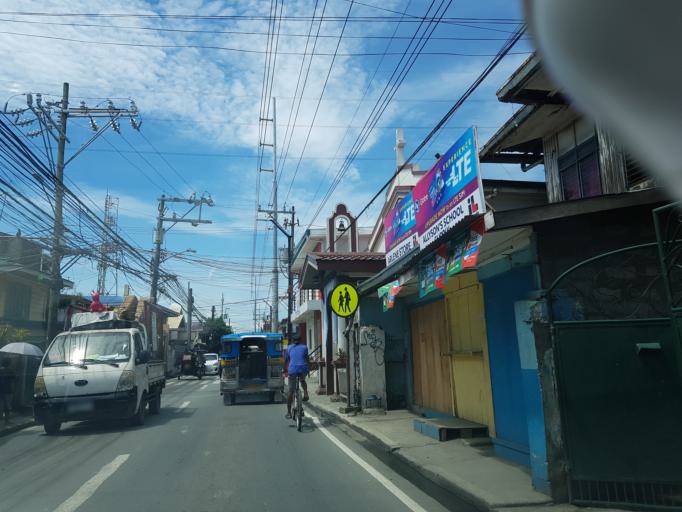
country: PH
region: Calabarzon
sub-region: Province of Rizal
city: Taguig
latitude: 14.5131
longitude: 121.0700
